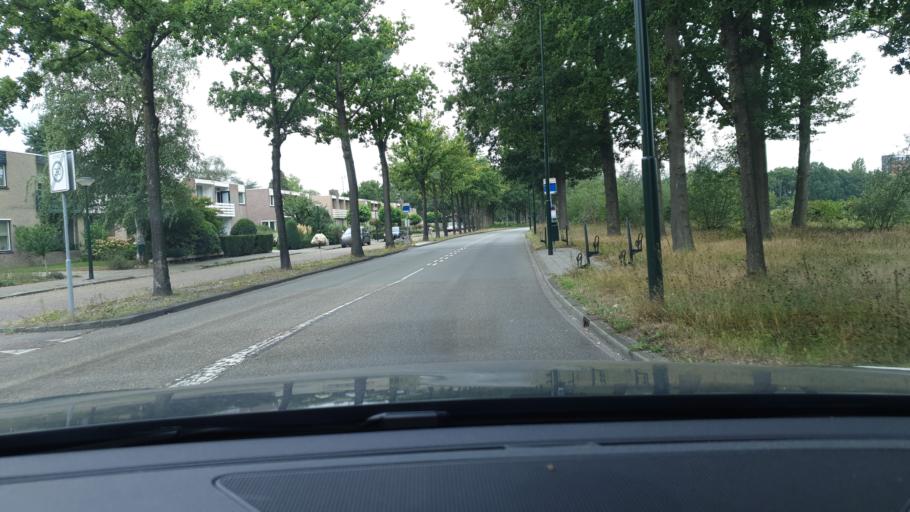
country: NL
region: North Brabant
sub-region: Gemeente Eindhoven
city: Lakerlopen
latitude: 51.4015
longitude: 5.4866
